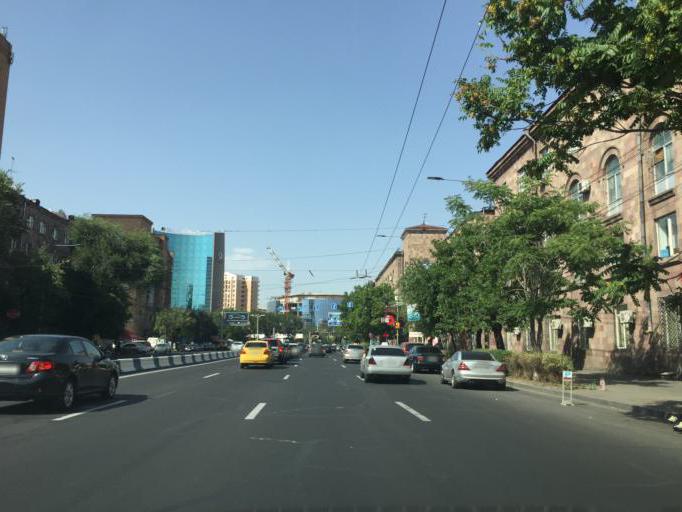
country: AM
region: Yerevan
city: Yerevan
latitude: 40.1692
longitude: 44.5075
